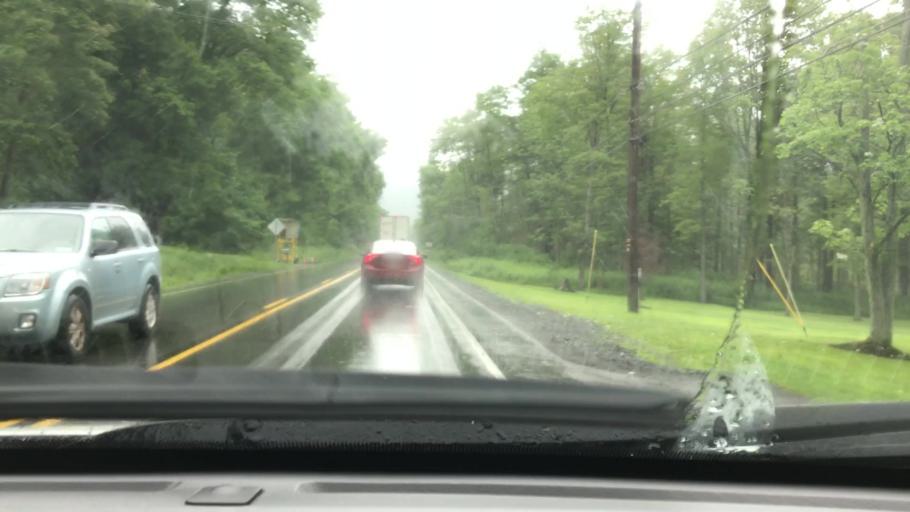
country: US
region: Pennsylvania
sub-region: Blair County
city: Tyrone
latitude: 40.7395
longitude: -78.1967
